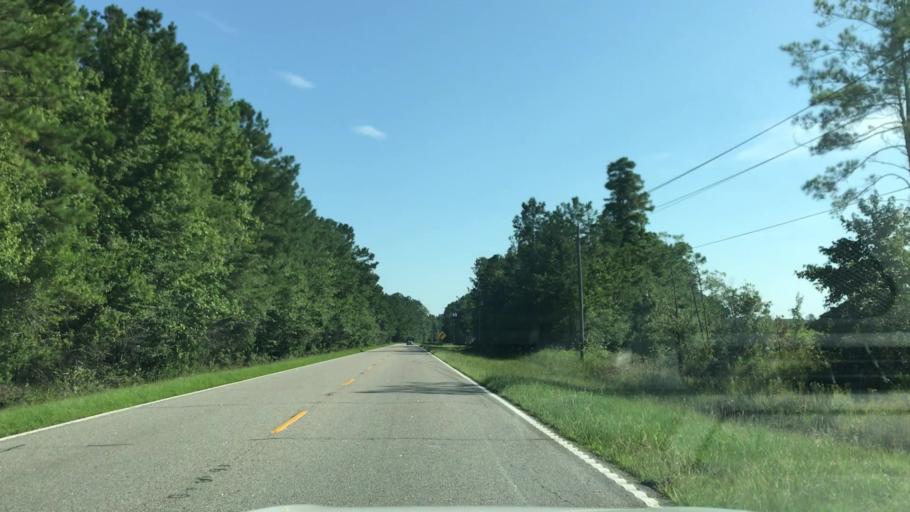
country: US
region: South Carolina
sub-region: Georgetown County
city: Georgetown
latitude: 33.5215
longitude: -79.2453
